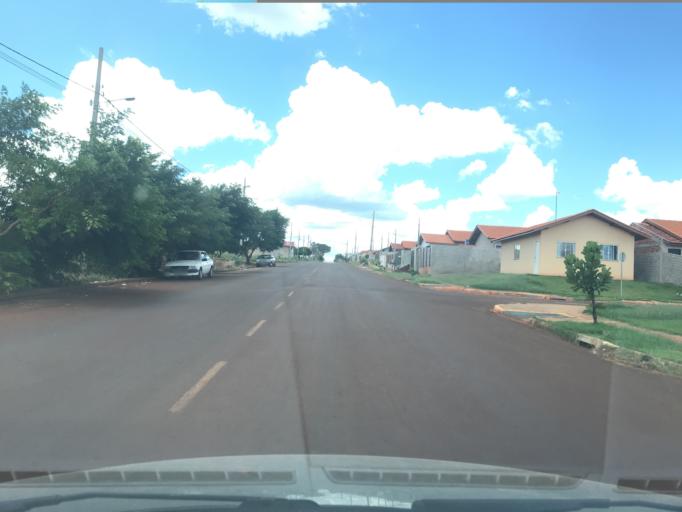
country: BR
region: Parana
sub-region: Palotina
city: Palotina
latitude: -24.2649
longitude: -53.8479
